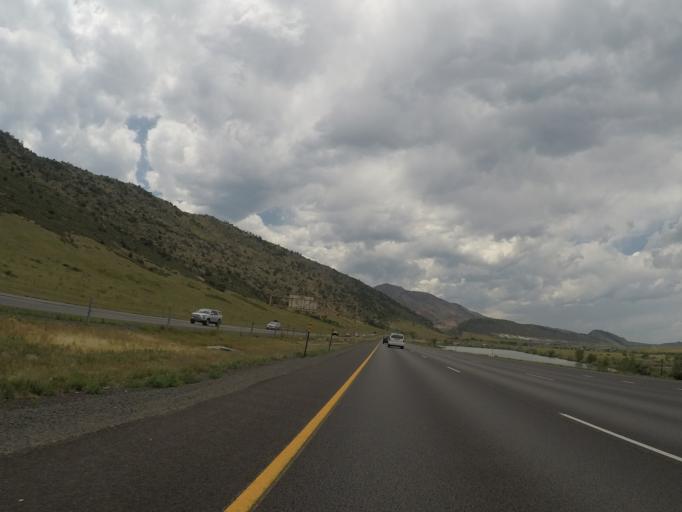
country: US
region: Colorado
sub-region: Jefferson County
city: Indian Hills
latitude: 39.6411
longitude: -105.1726
